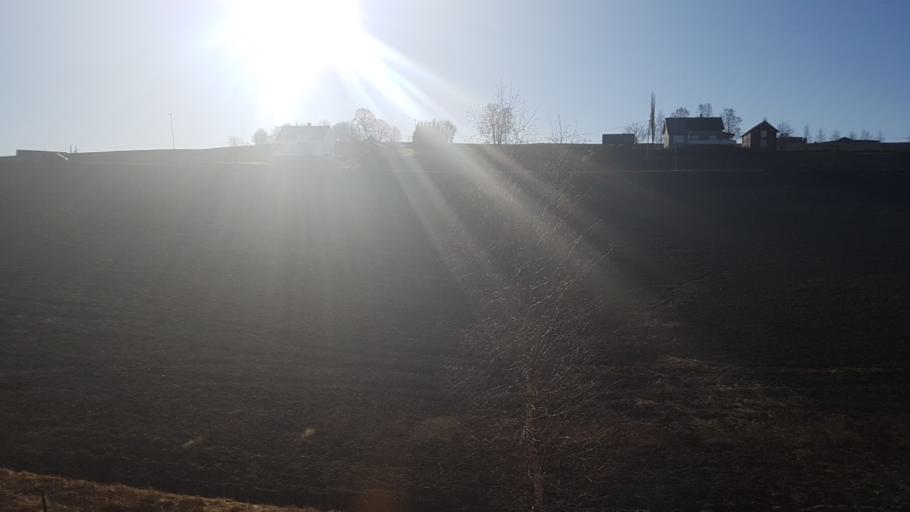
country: NO
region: Nord-Trondelag
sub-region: Levanger
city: Skogn
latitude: 63.6741
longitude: 11.1014
